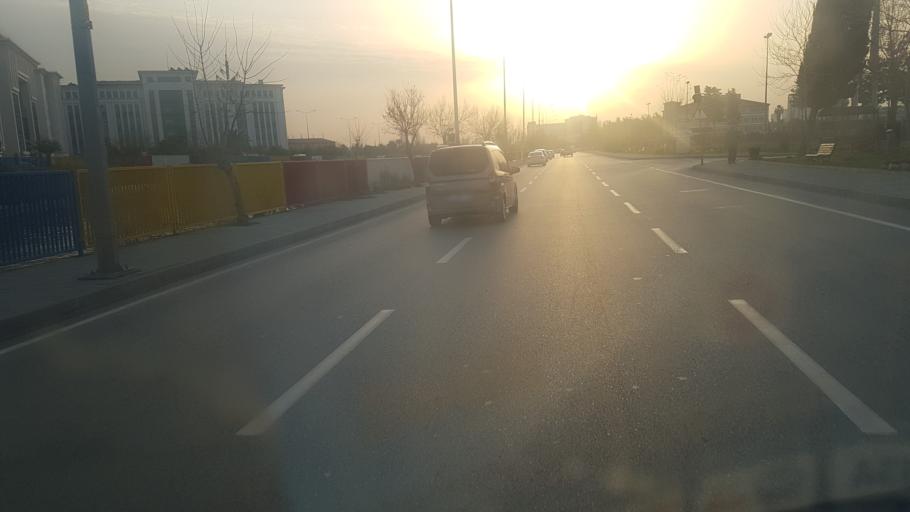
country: TR
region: Adana
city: Adana
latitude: 37.0131
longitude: 35.3444
